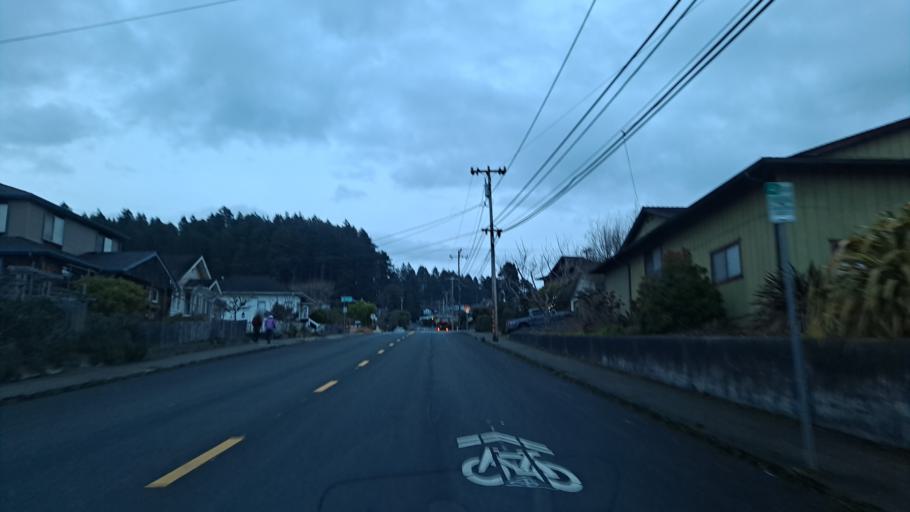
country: US
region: California
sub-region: Humboldt County
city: Arcata
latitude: 40.8690
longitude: -124.0790
